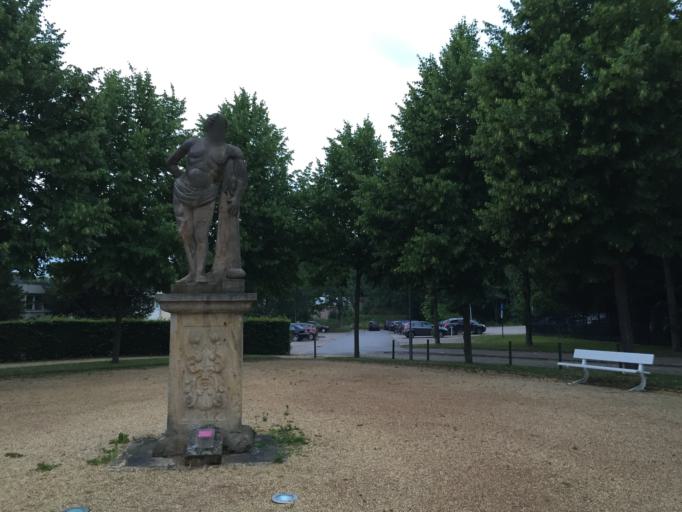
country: DE
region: Lower Saxony
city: Bad Pyrmont
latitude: 51.9881
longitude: 9.2523
